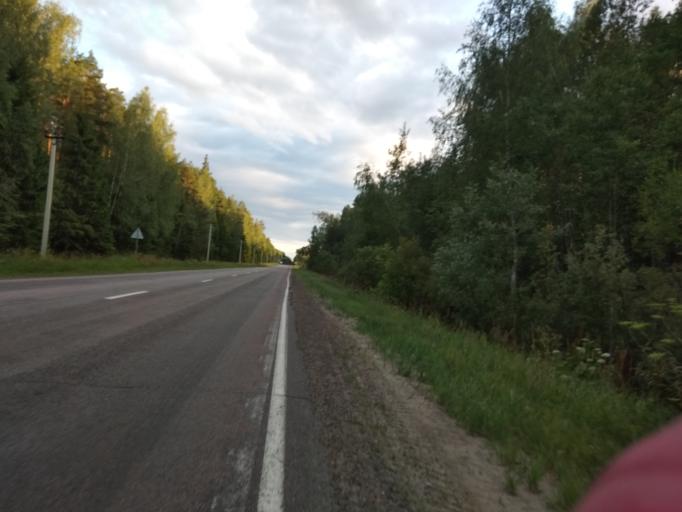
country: RU
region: Moskovskaya
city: Misheronskiy
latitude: 55.6228
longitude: 39.7315
